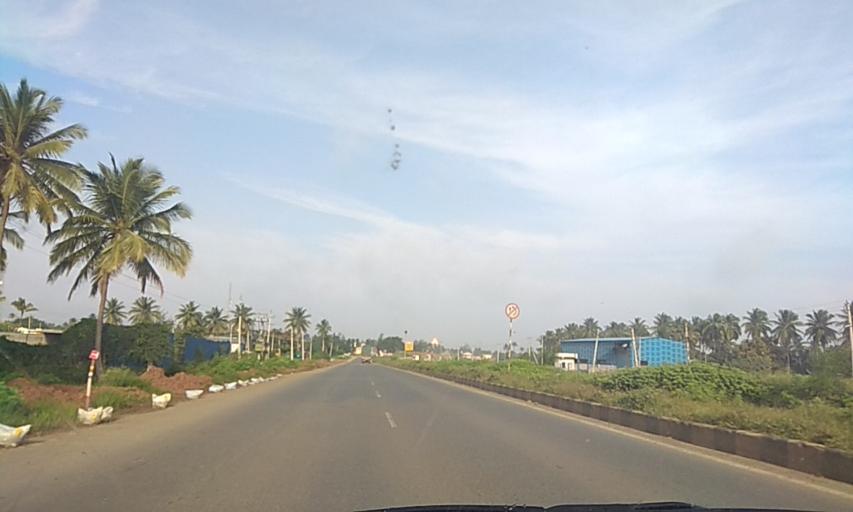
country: IN
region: Karnataka
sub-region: Haveri
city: Byadgi
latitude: 14.7168
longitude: 75.4871
